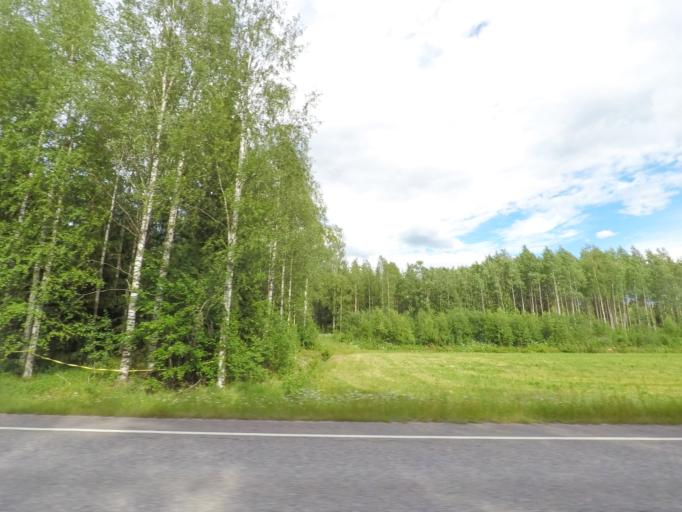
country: FI
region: Paijanne Tavastia
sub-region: Lahti
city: Hollola
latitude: 60.8303
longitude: 25.4901
